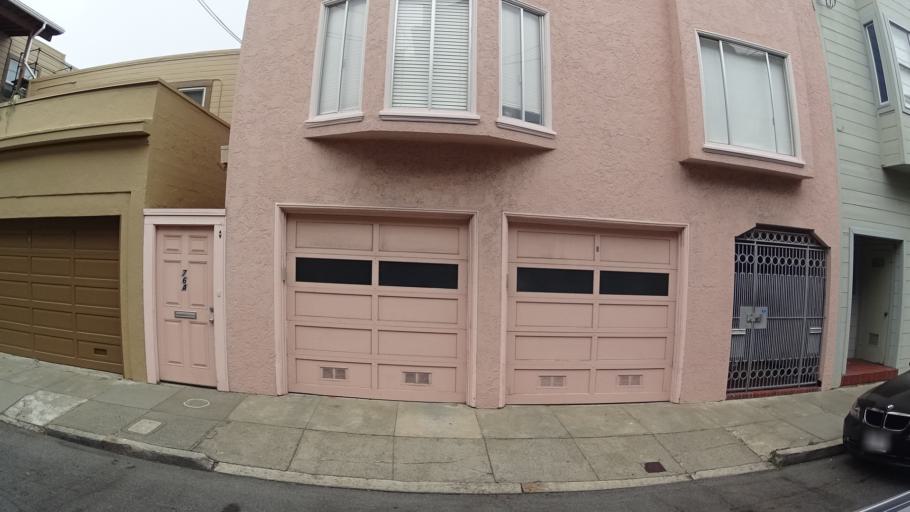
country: US
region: California
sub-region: San Francisco County
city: San Francisco
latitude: 37.7987
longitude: -122.4338
